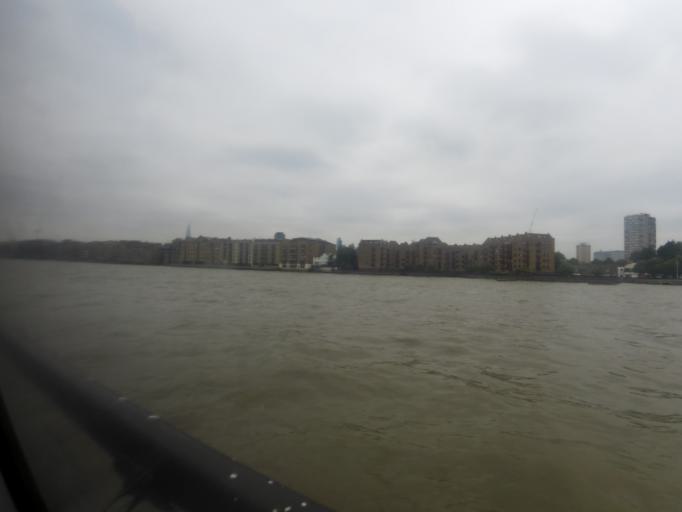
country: GB
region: England
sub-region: Greater London
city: Bethnal Green
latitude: 51.5065
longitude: -0.0482
